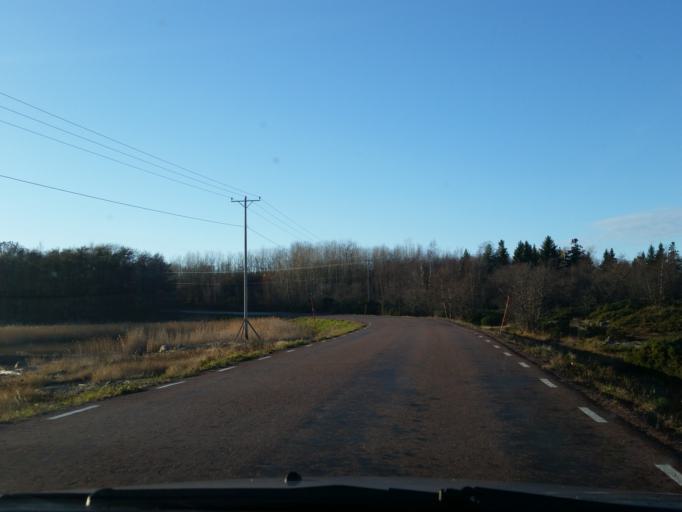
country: AX
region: Alands skaergard
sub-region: Braendoe
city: Braendoe
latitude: 60.4045
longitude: 21.0243
